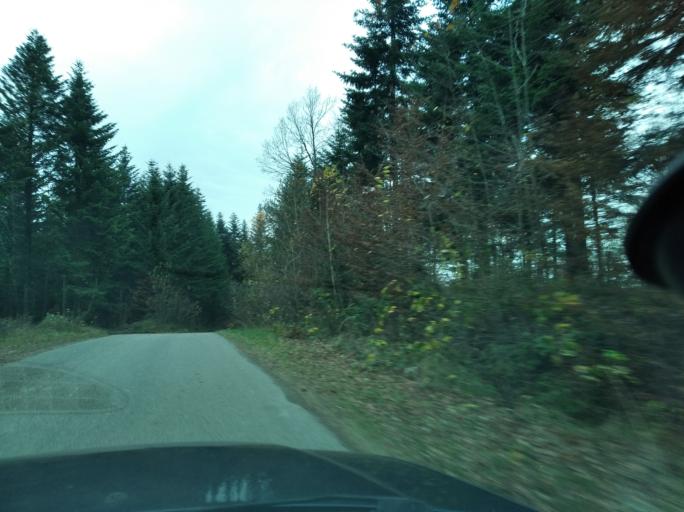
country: PL
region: Subcarpathian Voivodeship
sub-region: Powiat strzyzowski
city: Wysoka Strzyzowska
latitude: 49.8271
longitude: 21.7792
